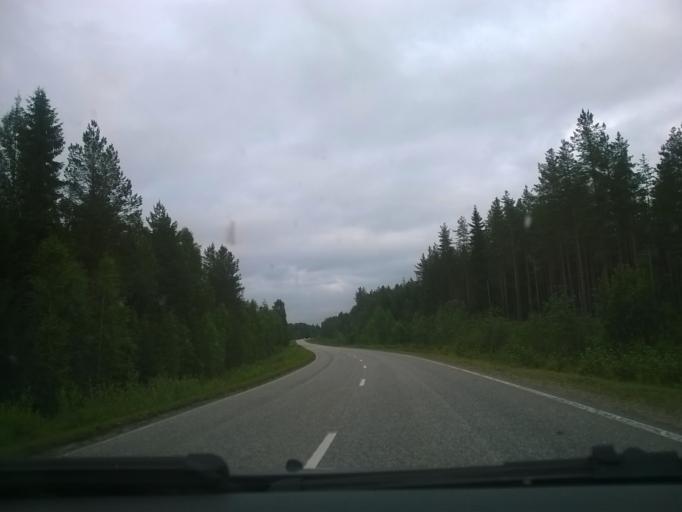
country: FI
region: Kainuu
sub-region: Kehys-Kainuu
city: Kuhmo
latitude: 64.1452
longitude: 29.4245
